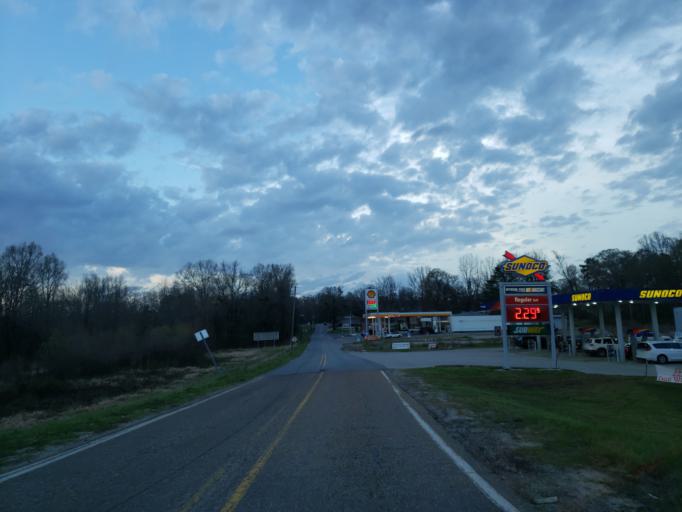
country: US
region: Mississippi
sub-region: Lauderdale County
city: Marion
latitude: 32.4144
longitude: -88.5062
